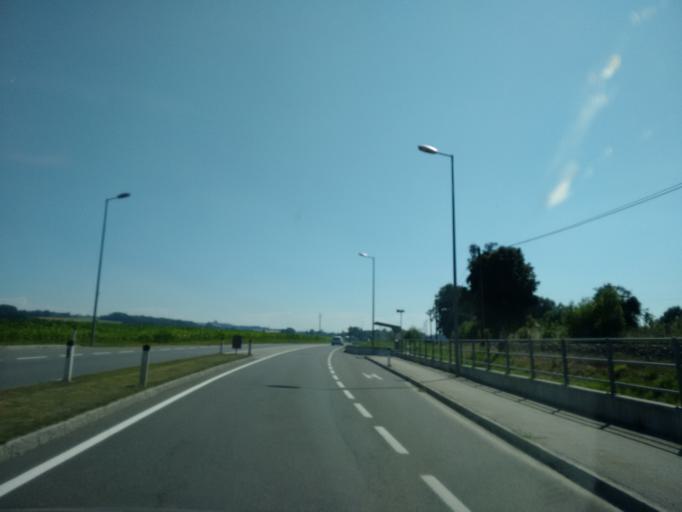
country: AT
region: Upper Austria
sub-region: Wels-Land
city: Buchkirchen
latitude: 48.2888
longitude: 14.0090
